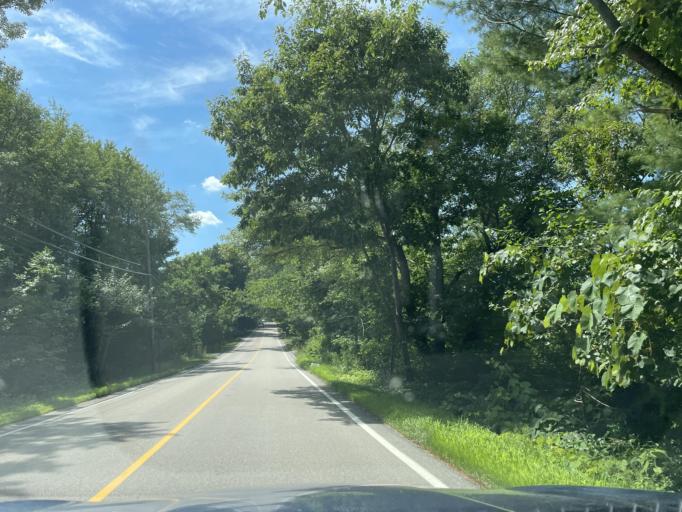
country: US
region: Massachusetts
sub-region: Middlesex County
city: Sherborn
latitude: 42.2364
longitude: -71.4009
